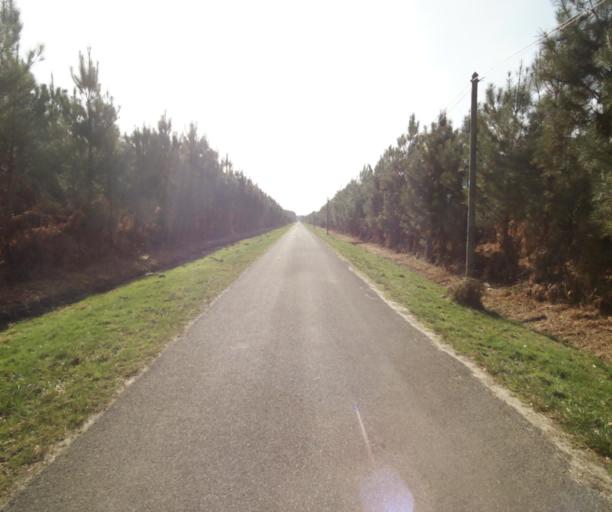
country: FR
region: Aquitaine
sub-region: Departement des Landes
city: Roquefort
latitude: 44.1456
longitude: -0.1749
